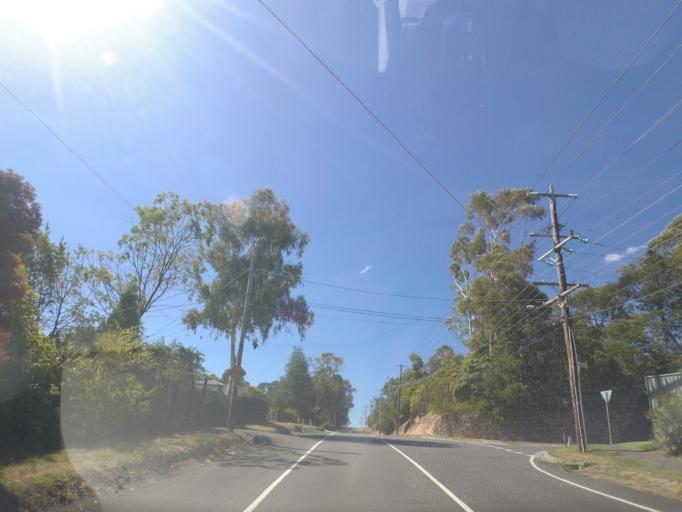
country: AU
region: Victoria
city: Mitcham
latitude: -37.8011
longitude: 145.2155
